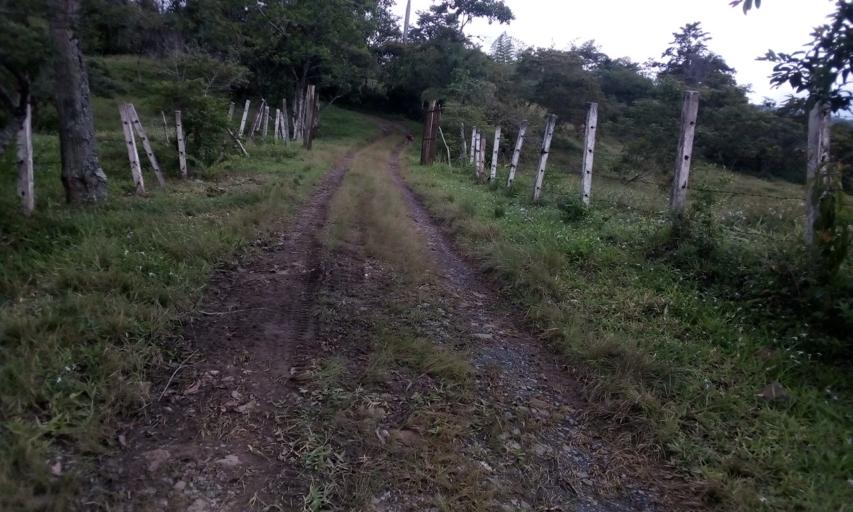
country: CO
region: Santander
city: Guepsa
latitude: 6.0198
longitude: -73.5304
